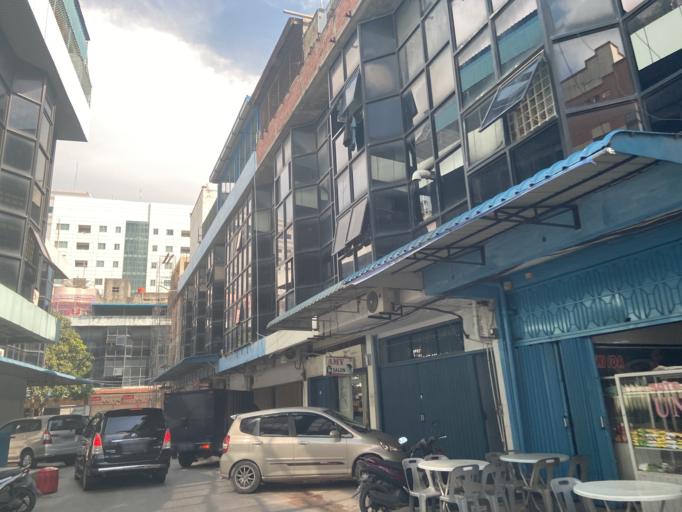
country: SG
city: Singapore
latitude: 1.1501
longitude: 104.0060
